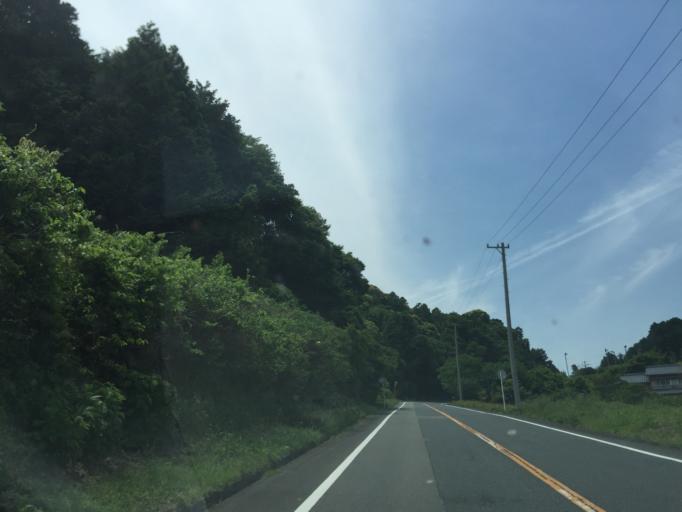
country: JP
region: Shizuoka
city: Kakegawa
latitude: 34.7928
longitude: 138.0064
